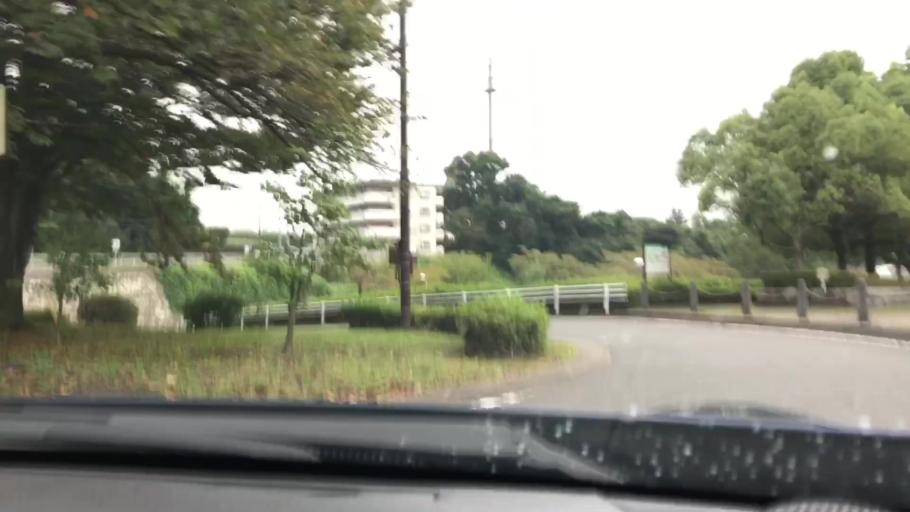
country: JP
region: Gunma
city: Kanekomachi
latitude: 36.3997
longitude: 138.9508
